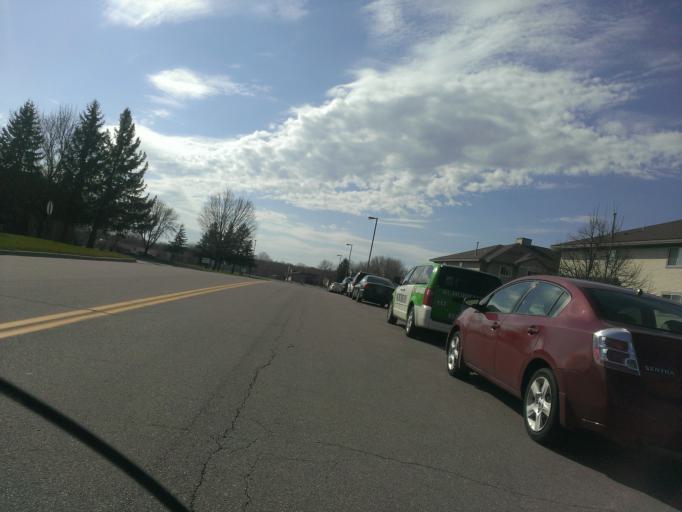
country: US
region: Minnesota
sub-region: Scott County
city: Savage
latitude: 44.7478
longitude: -93.3315
